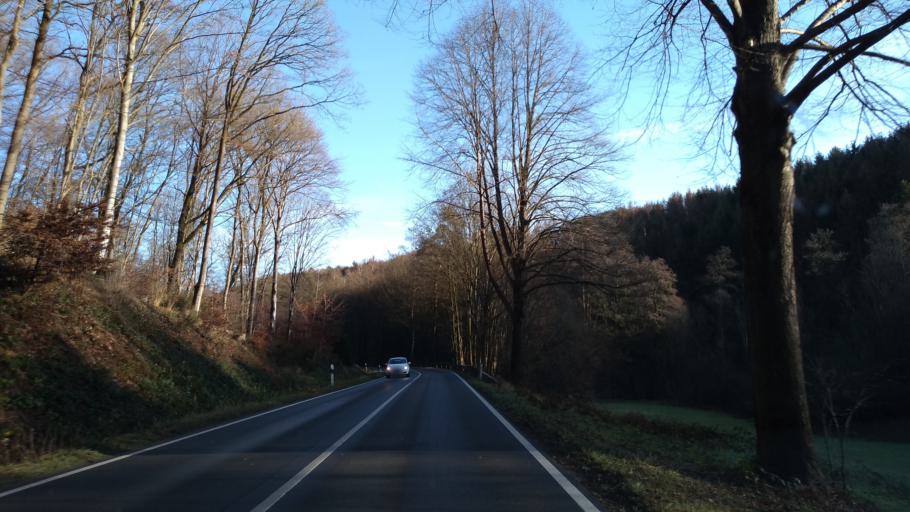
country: DE
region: North Rhine-Westphalia
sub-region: Regierungsbezirk Koln
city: Overath
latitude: 50.8550
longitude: 7.3211
